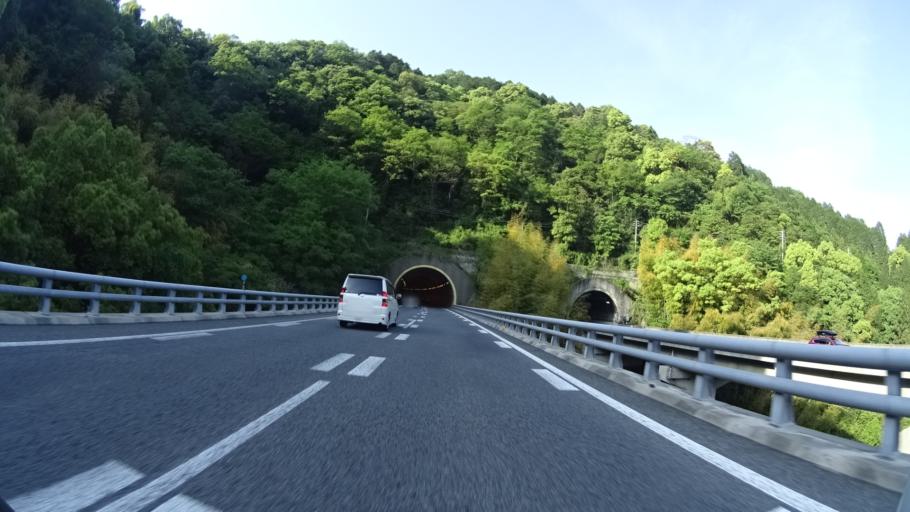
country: JP
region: Ehime
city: Saijo
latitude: 33.8909
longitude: 133.1969
